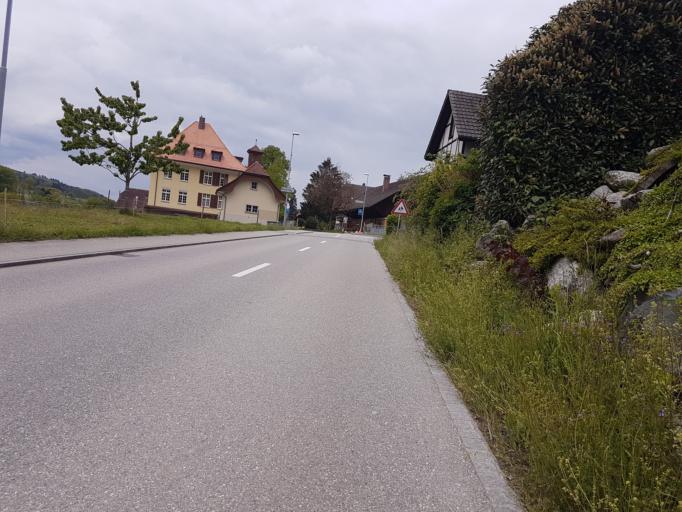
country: CH
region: Bern
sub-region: Oberaargau
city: Niederbipp
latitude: 47.2359
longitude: 7.6923
